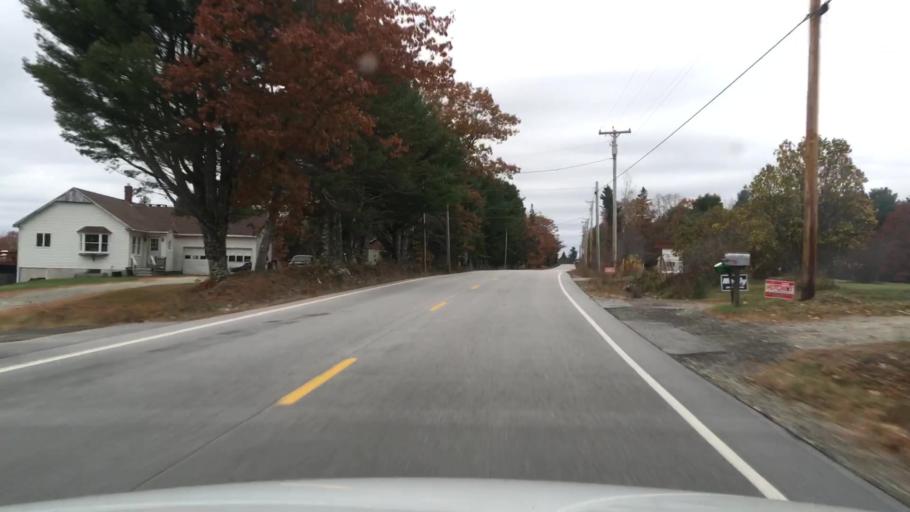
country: US
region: Maine
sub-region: Hancock County
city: Orland
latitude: 44.5417
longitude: -68.6844
